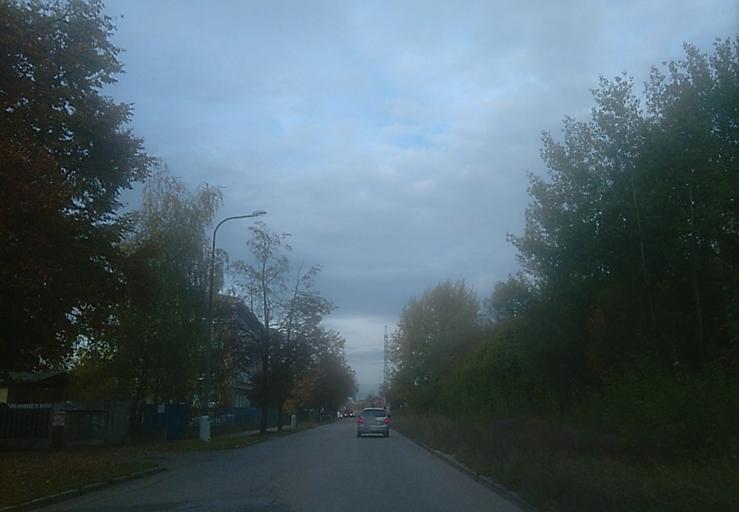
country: CZ
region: Jihocesky
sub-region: Okres Ceske Budejovice
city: Ceske Budejovice
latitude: 48.9755
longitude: 14.5029
